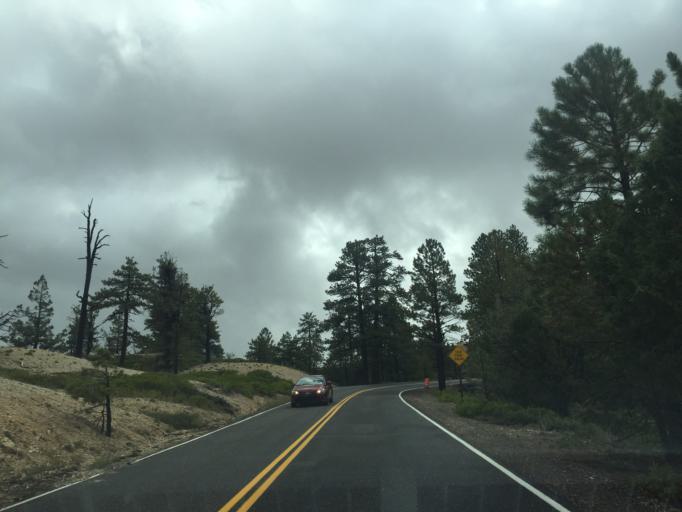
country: US
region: Utah
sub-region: Garfield County
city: Panguitch
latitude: 37.6161
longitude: -112.1718
